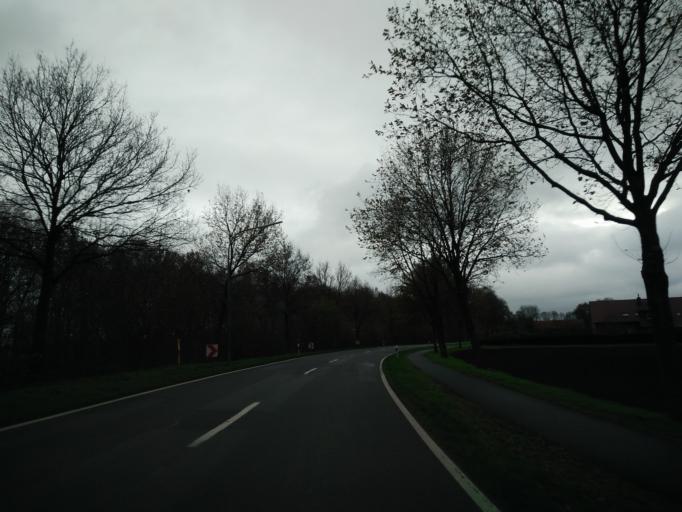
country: NL
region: Drenthe
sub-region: Gemeente Emmen
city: Emmer-Compascuum
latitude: 52.8005
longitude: 7.1094
